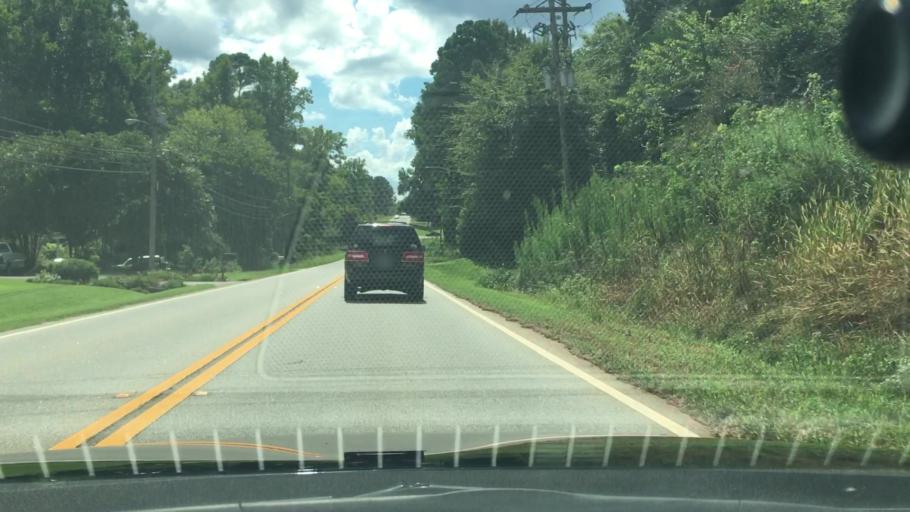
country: US
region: Georgia
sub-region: Putnam County
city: Eatonton
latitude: 33.3214
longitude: -83.4017
